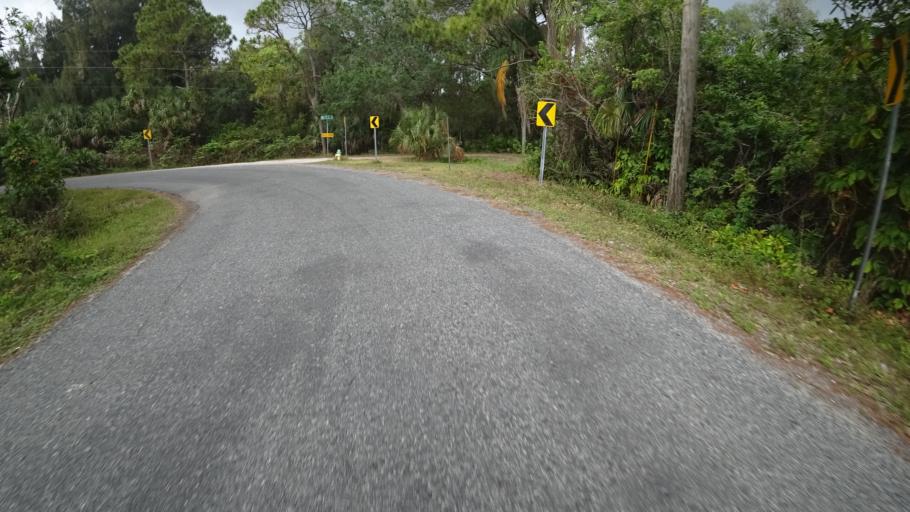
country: US
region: Florida
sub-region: Manatee County
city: Samoset
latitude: 27.4797
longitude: -82.5034
